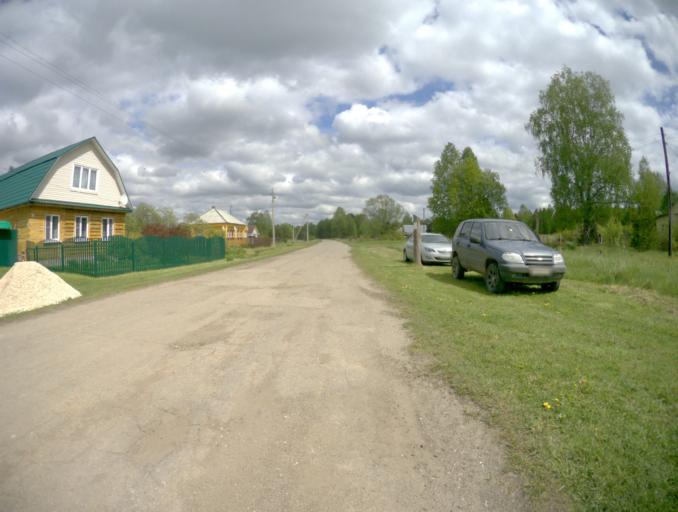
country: RU
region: Rjazan
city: Gus'-Zheleznyy
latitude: 55.1179
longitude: 40.9251
